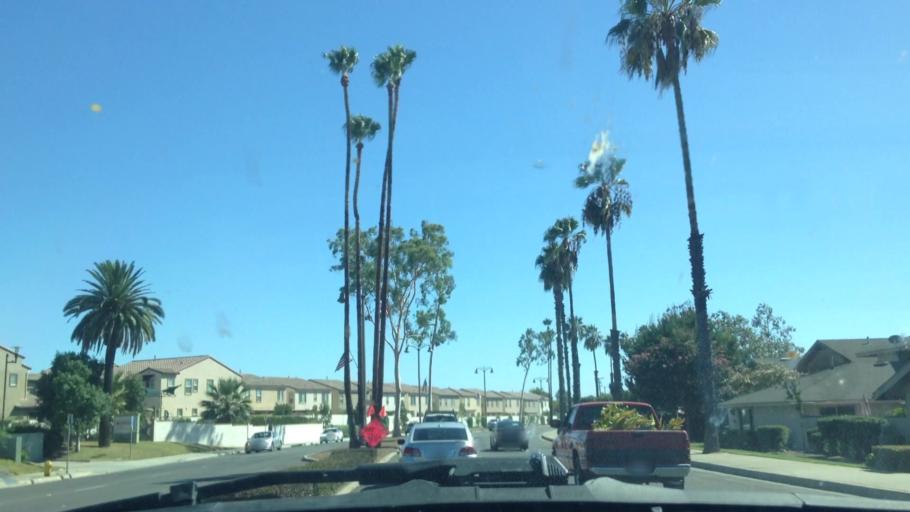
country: US
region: California
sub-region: Orange County
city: Placentia
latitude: 33.8850
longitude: -117.8629
